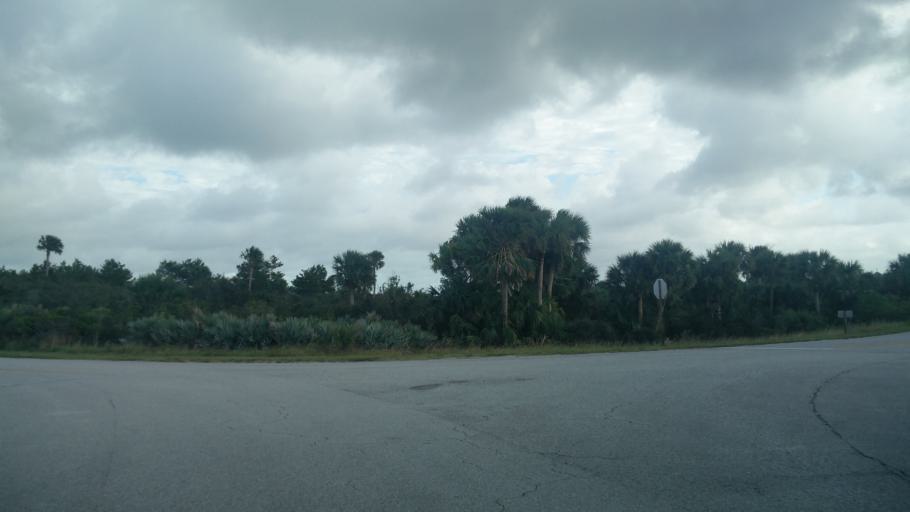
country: US
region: Florida
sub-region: Palm Beach County
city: Tequesta
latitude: 27.0037
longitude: -80.1030
